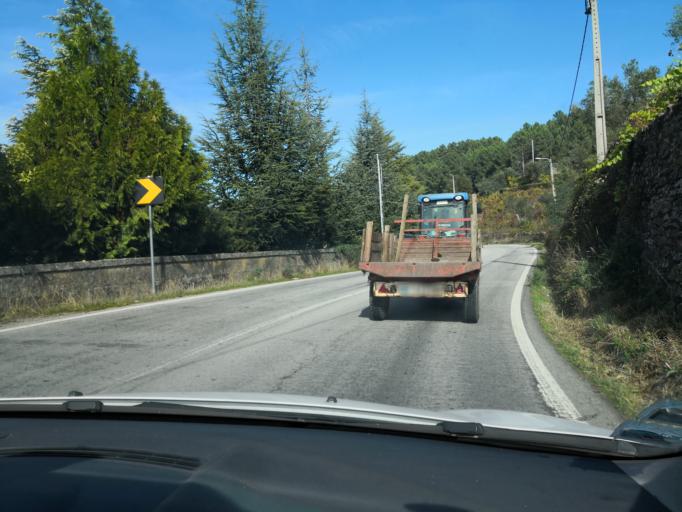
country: PT
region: Vila Real
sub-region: Vila Real
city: Vila Real
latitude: 41.2920
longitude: -7.7071
